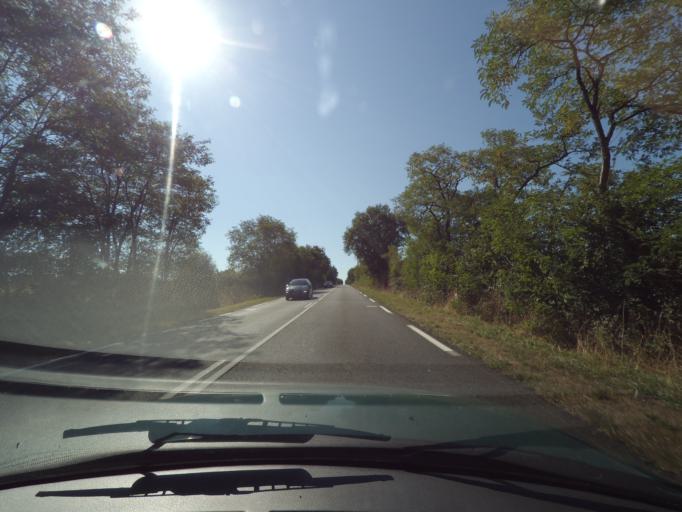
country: FR
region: Poitou-Charentes
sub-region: Departement de la Vienne
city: Lussac-les-Chateaux
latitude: 46.3616
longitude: 0.7745
